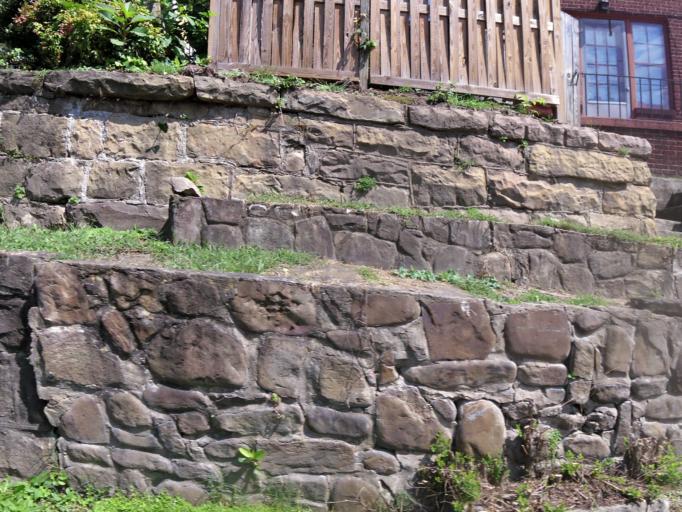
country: US
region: Kentucky
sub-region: Harlan County
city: Harlan
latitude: 36.8495
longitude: -83.3226
